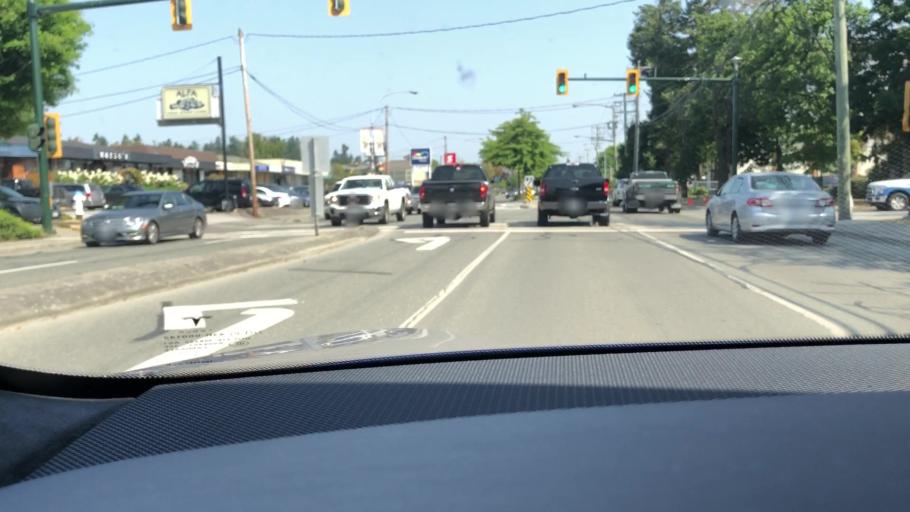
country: US
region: Washington
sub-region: Whatcom County
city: Point Roberts
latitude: 49.0224
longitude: -123.0686
